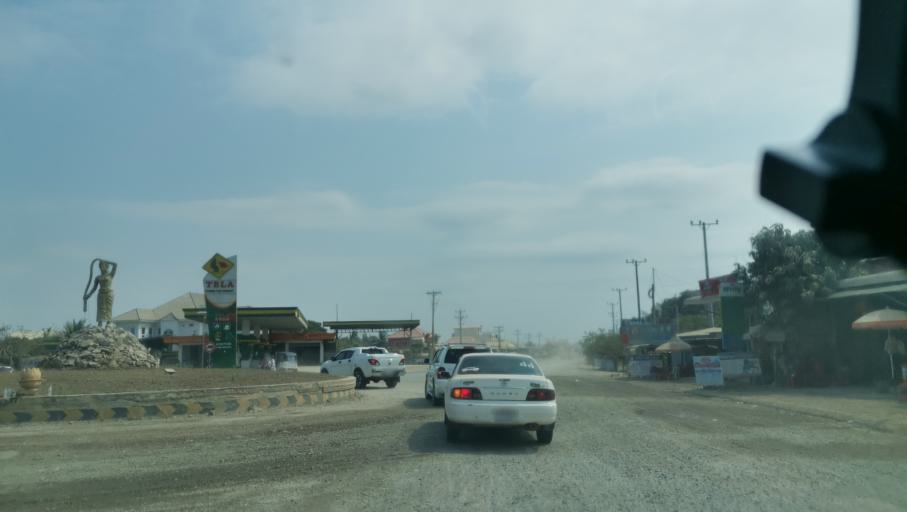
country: KH
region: Battambang
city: Battambang
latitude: 13.0759
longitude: 103.1796
